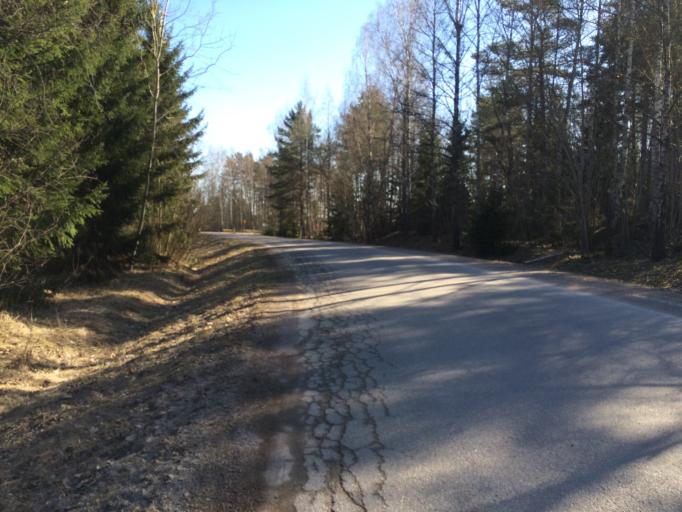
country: SE
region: Vaestmanland
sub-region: Hallstahammars Kommun
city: Hallstahammar
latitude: 59.5940
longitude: 16.2442
